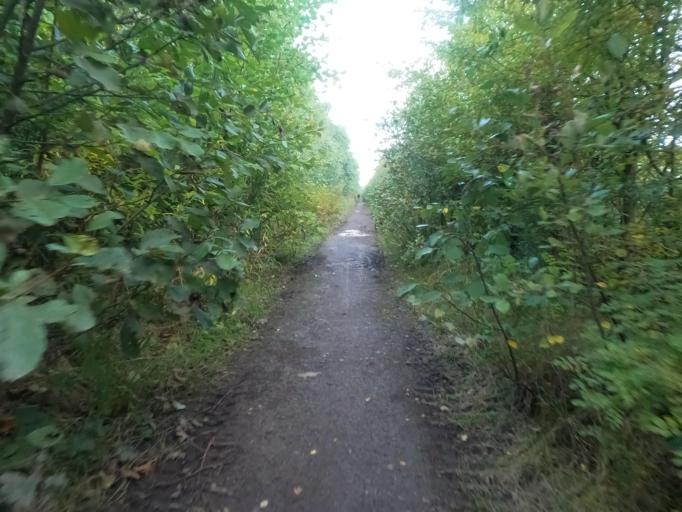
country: GB
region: England
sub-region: Northumberland
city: Seghill
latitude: 55.0700
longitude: -1.5470
